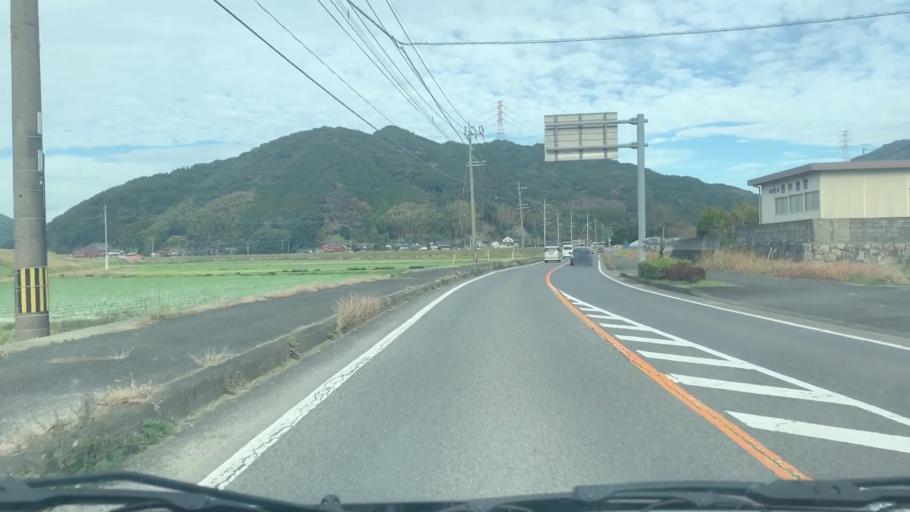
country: JP
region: Saga Prefecture
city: Karatsu
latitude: 33.3754
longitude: 130.0000
